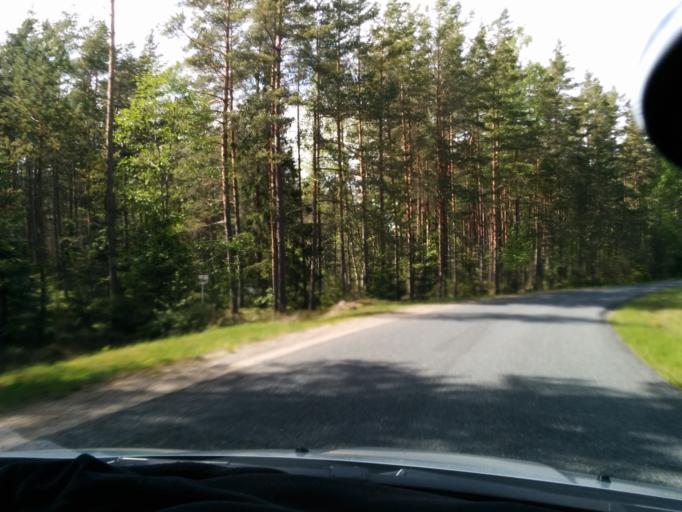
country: EE
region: Harju
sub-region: Loksa linn
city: Loksa
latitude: 59.5674
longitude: 25.6257
